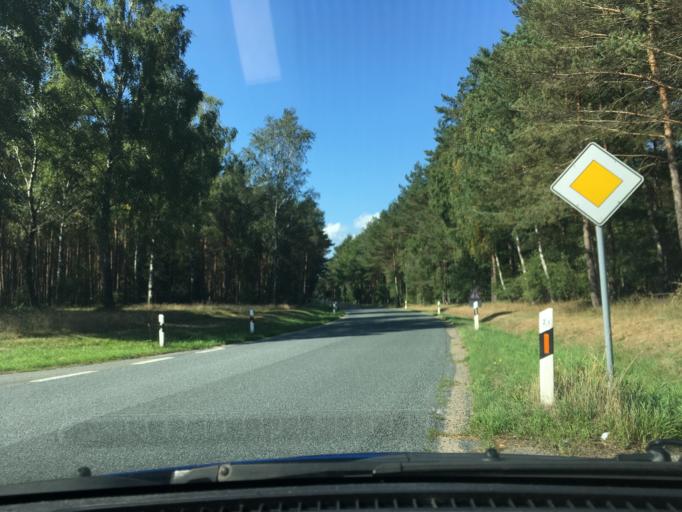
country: DE
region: Lower Saxony
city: Wietzendorf
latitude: 52.8911
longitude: 10.0144
